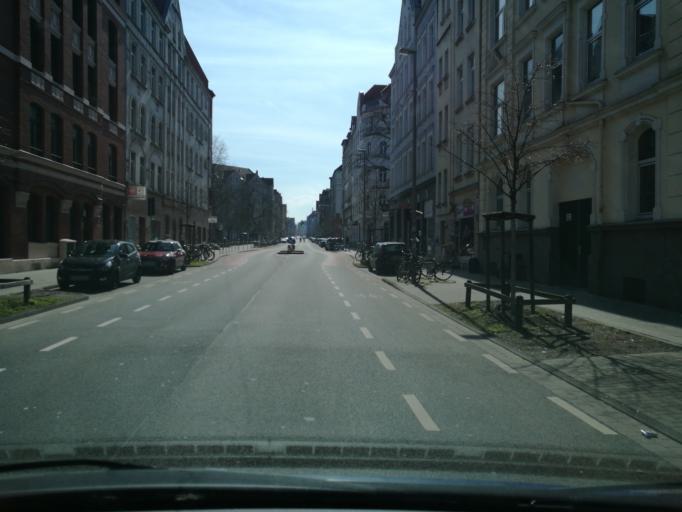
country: DE
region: Lower Saxony
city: Hannover
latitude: 52.3732
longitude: 9.7046
